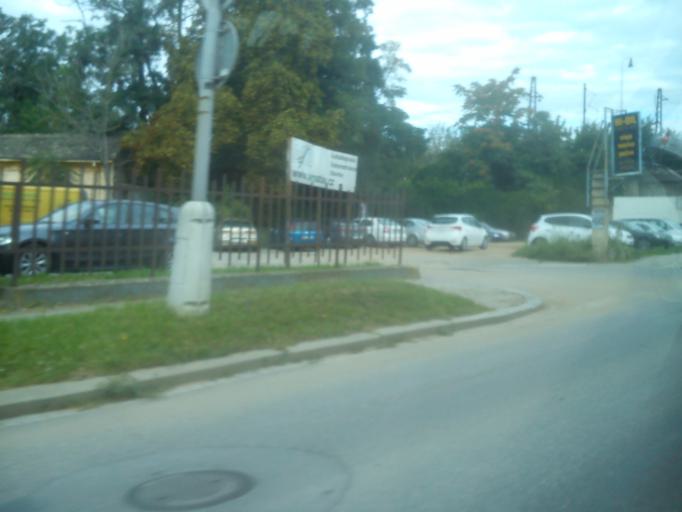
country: CZ
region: South Moravian
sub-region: Mesto Brno
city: Brno
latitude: 49.1844
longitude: 16.6187
